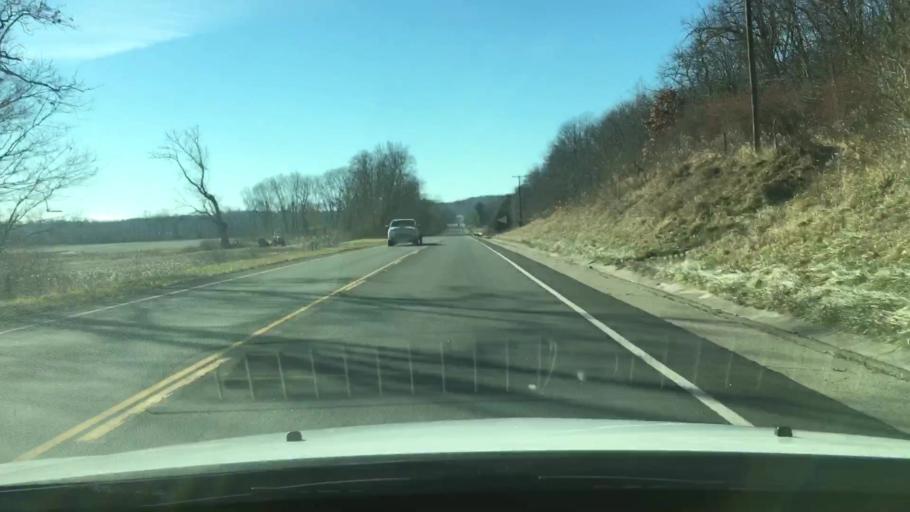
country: US
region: Illinois
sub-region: Fulton County
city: Canton
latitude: 40.5007
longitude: -89.9303
